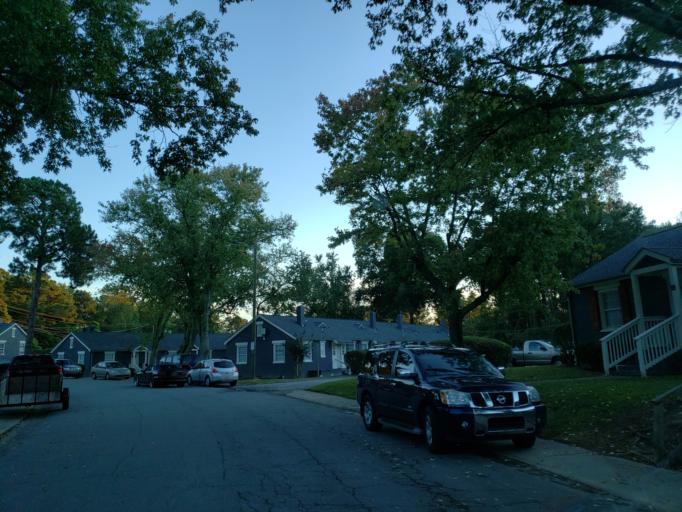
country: US
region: Georgia
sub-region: Cobb County
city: Marietta
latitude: 33.9461
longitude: -84.5253
